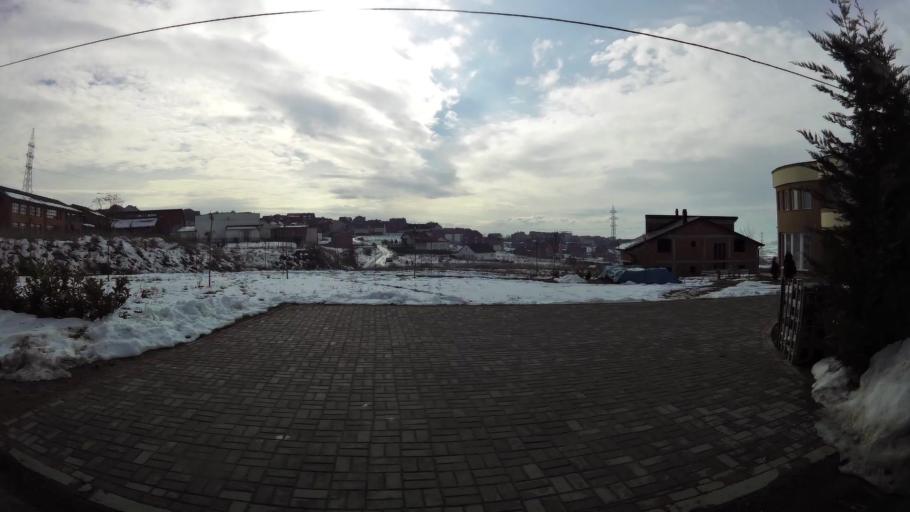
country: XK
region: Pristina
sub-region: Komuna e Prishtines
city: Pristina
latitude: 42.6884
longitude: 21.1559
